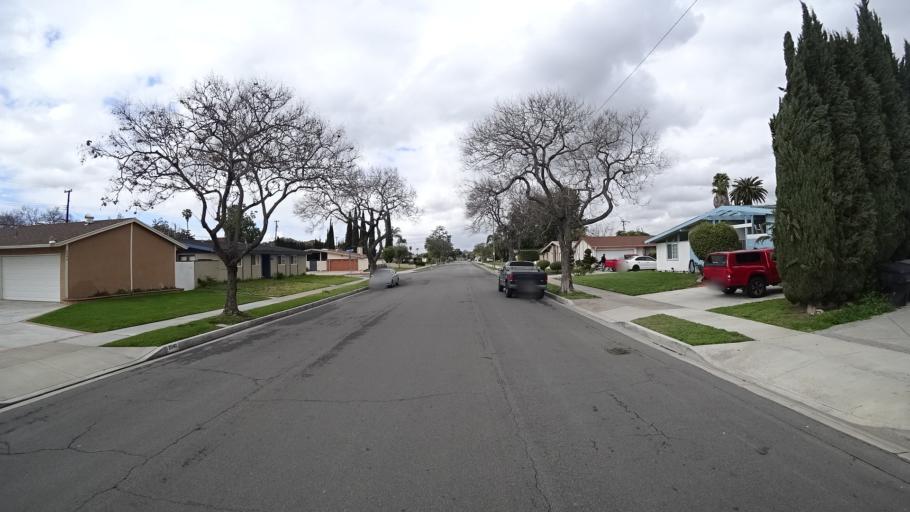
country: US
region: California
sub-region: Orange County
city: Stanton
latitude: 33.8195
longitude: -117.9541
